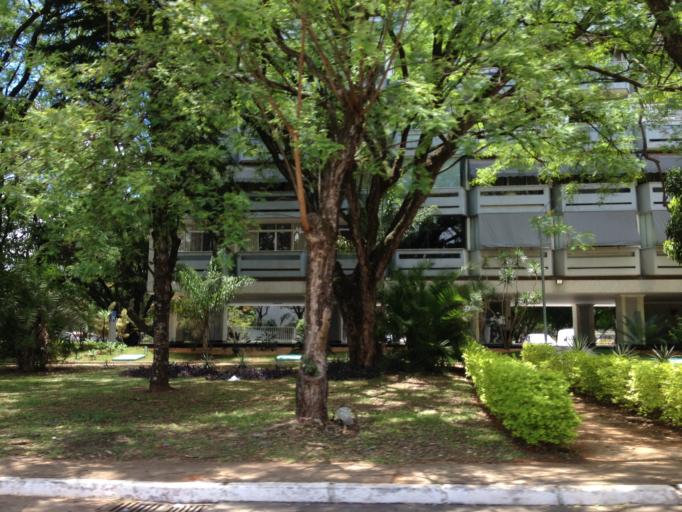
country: BR
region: Federal District
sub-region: Brasilia
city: Brasilia
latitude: -15.8206
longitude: -47.9165
